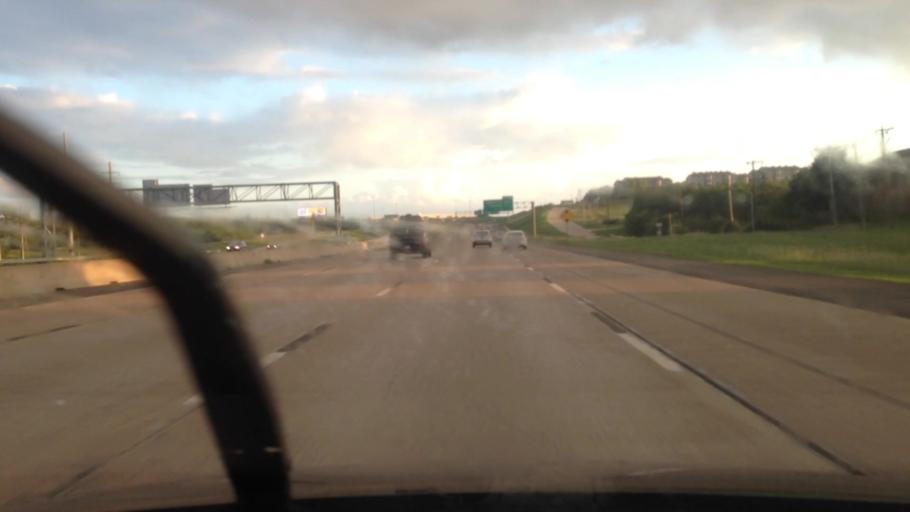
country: US
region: Texas
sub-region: Tarrant County
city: White Settlement
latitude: 32.7538
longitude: -97.4799
